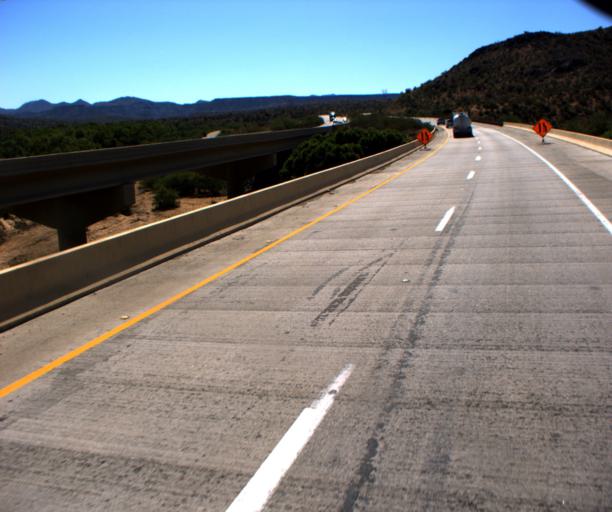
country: US
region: Arizona
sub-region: Yavapai County
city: Bagdad
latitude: 34.3690
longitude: -113.1855
